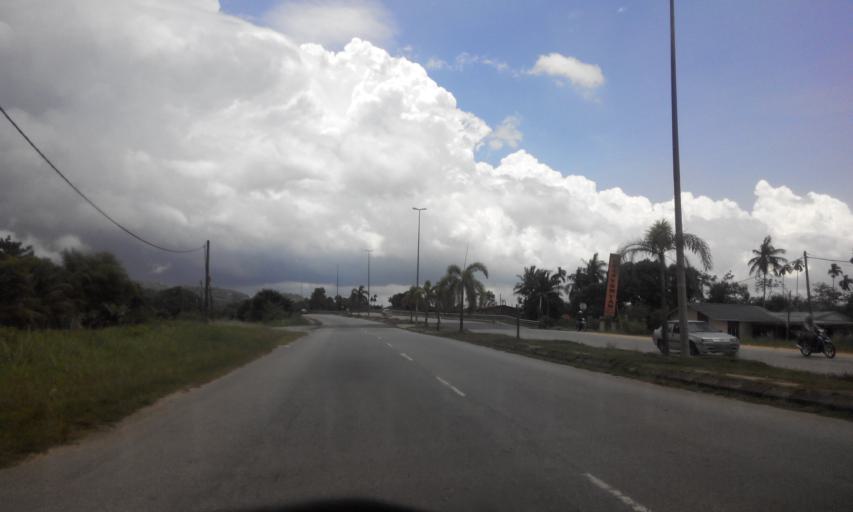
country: MY
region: Perak
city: Parit Buntar
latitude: 5.1280
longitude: 100.5040
